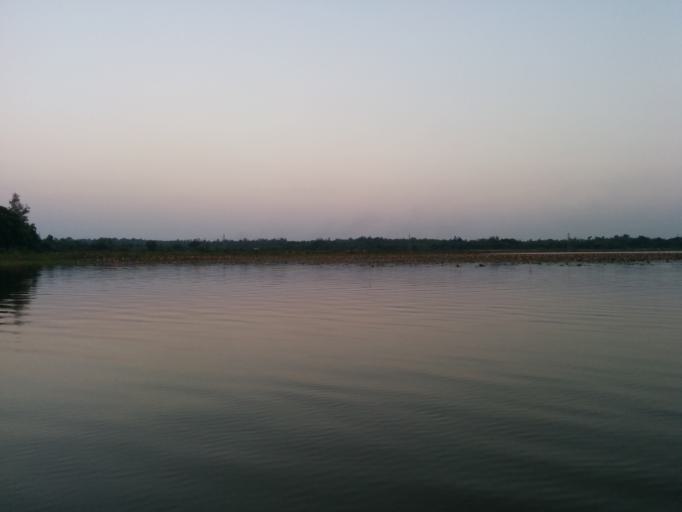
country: IN
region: Tamil Nadu
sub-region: Villupuram
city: Auroville
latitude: 11.9553
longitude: 79.7518
